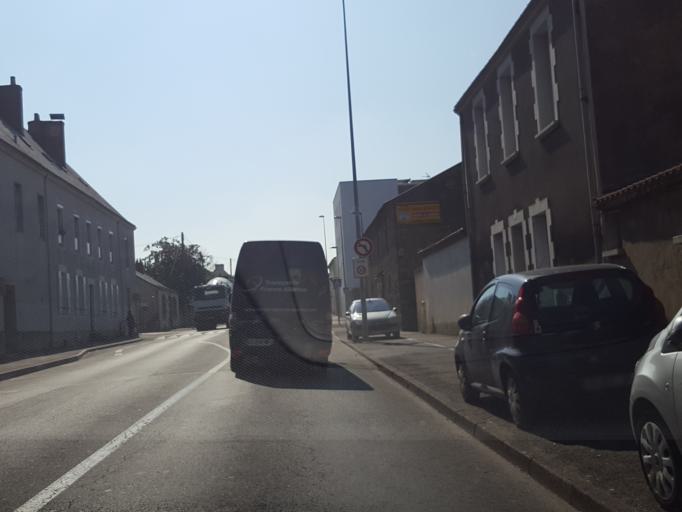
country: FR
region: Pays de la Loire
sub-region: Departement de la Vendee
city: La Roche-sur-Yon
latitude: 46.6618
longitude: -1.4223
